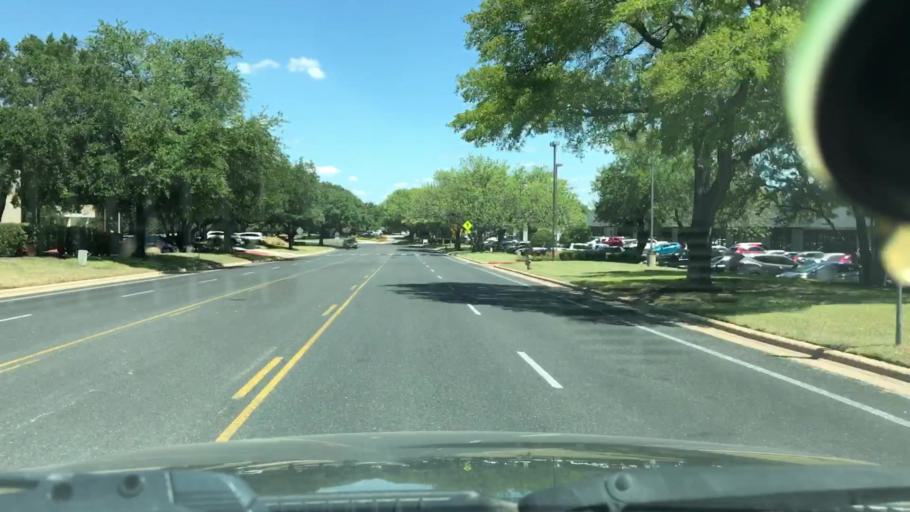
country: US
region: Texas
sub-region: Williamson County
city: Jollyville
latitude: 30.4318
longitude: -97.7609
